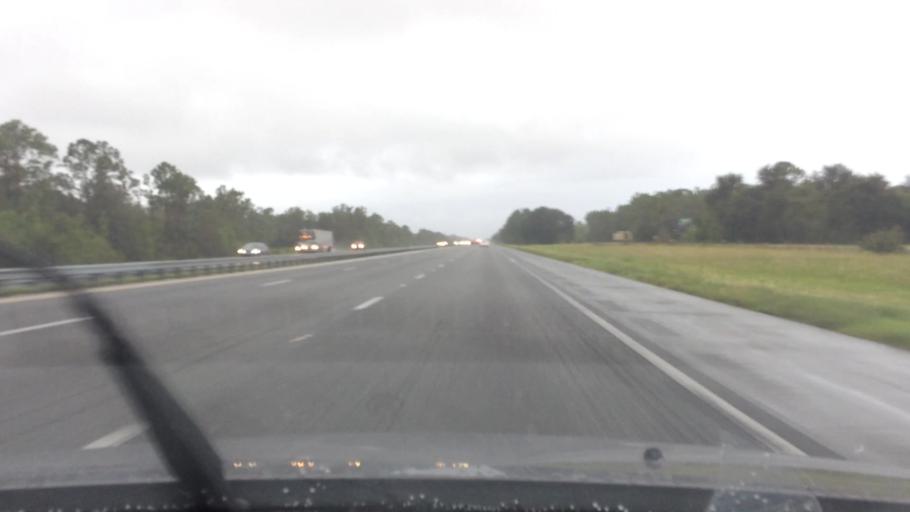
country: US
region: Florida
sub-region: Volusia County
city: Ormond Beach
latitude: 29.3051
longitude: -81.1317
